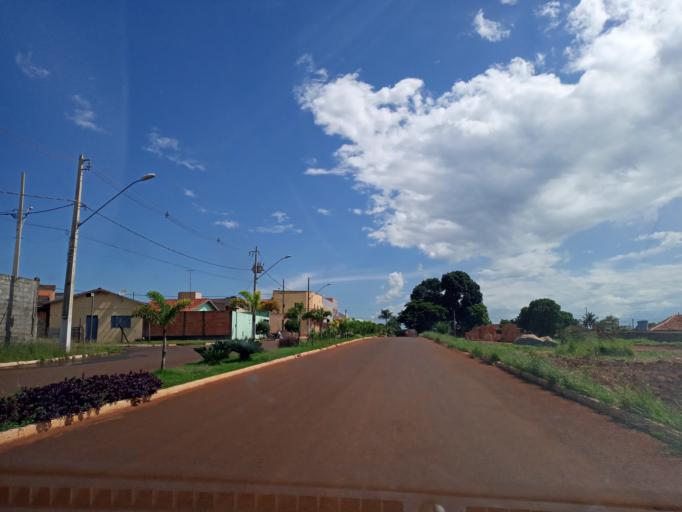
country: BR
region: Goias
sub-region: Itumbiara
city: Itumbiara
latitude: -18.4355
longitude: -49.1824
